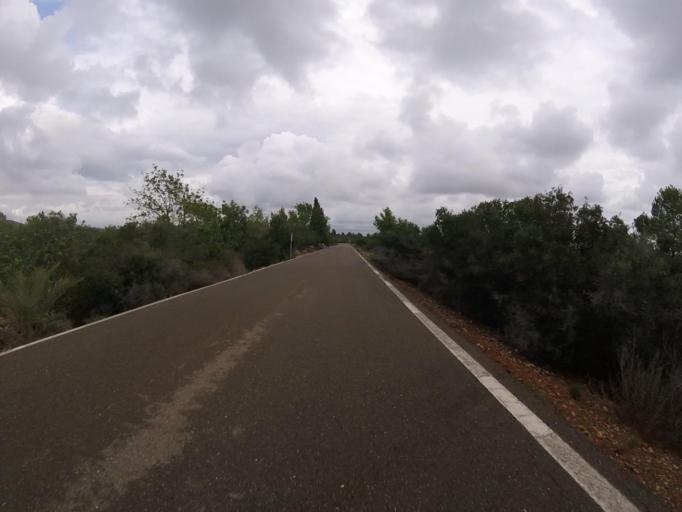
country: ES
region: Valencia
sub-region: Provincia de Castello
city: Torreblanca
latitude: 40.2301
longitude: 0.1315
